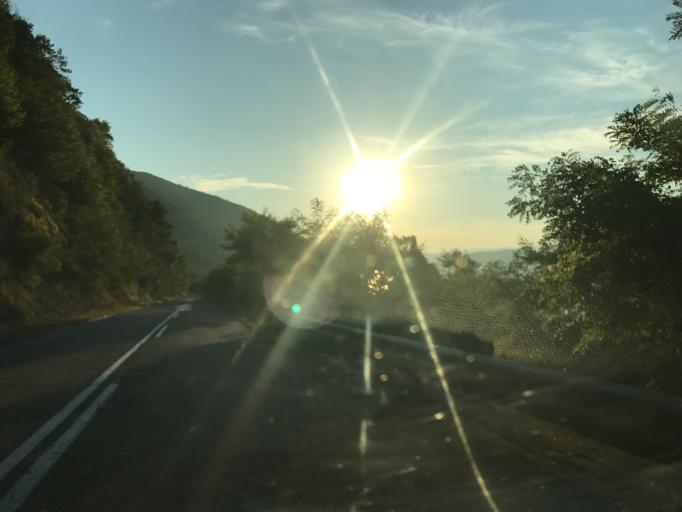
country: RO
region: Caras-Severin
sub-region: Comuna Berzasca
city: Berzasca
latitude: 44.6295
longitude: 21.9666
